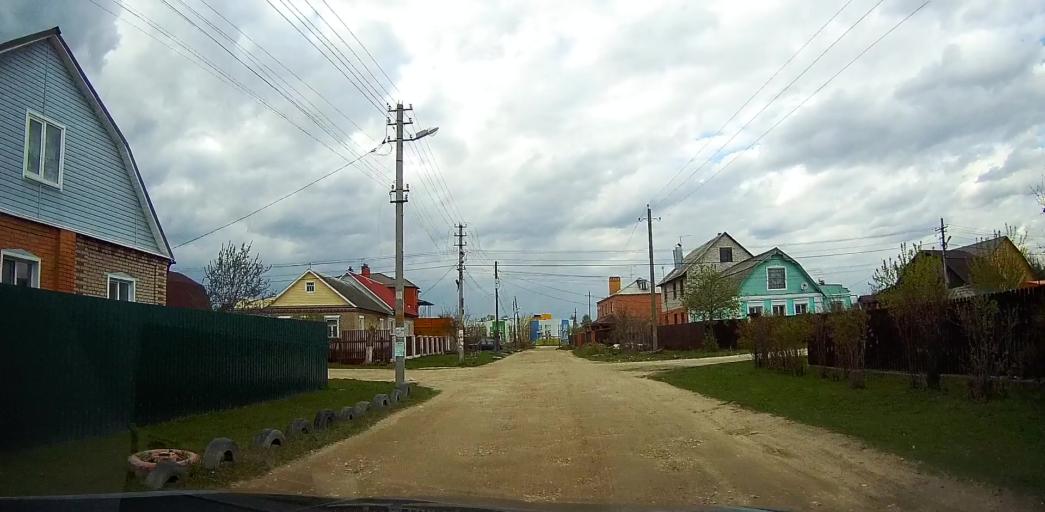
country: RU
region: Moskovskaya
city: Pavlovskiy Posad
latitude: 55.7791
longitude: 38.6313
